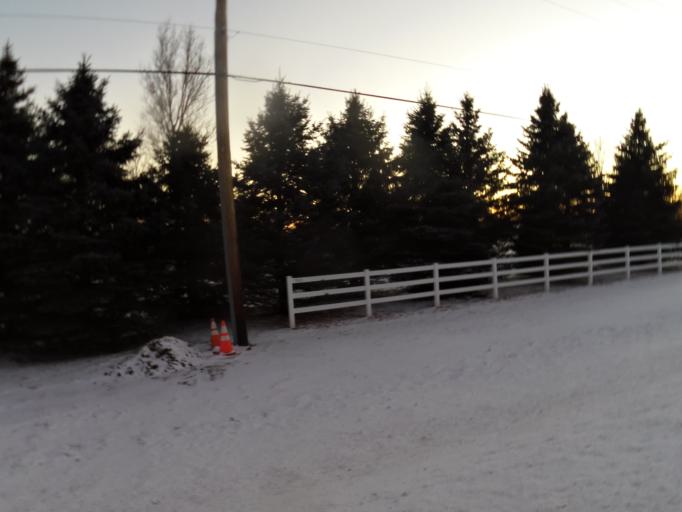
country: US
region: Minnesota
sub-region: Washington County
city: Lakeland
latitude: 44.9629
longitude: -92.8168
